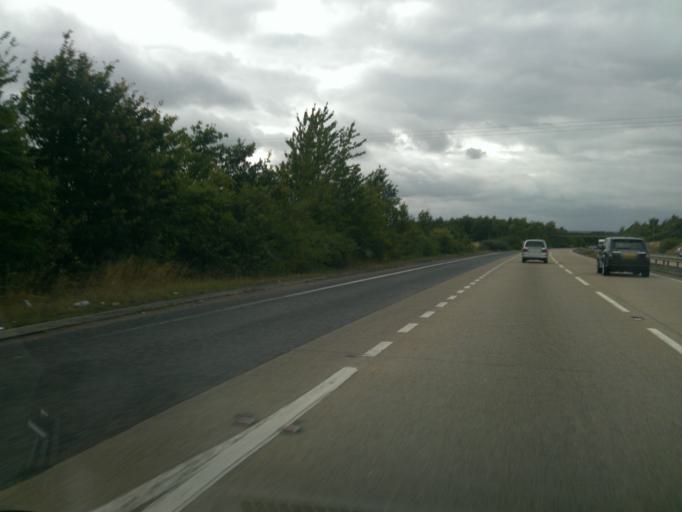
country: GB
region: England
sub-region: Essex
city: Wivenhoe
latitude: 51.9023
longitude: 0.9760
